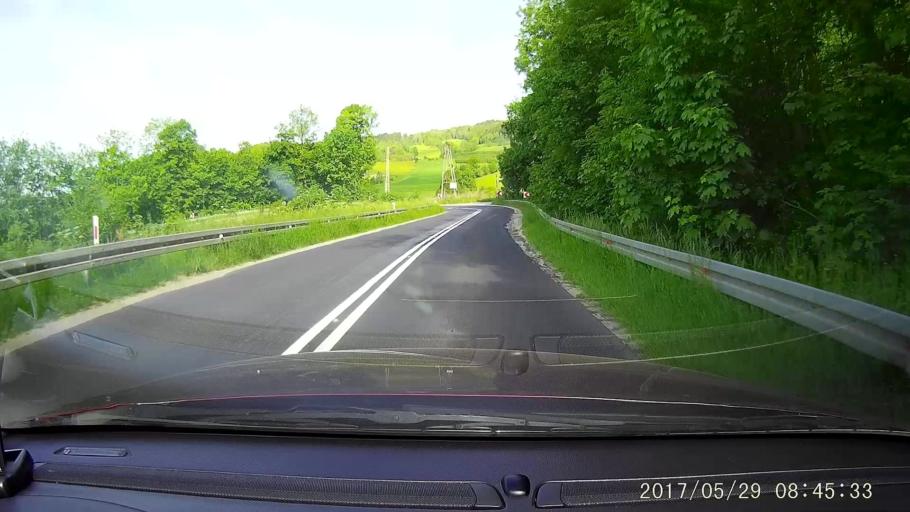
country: PL
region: Lower Silesian Voivodeship
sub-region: Powiat jeleniogorski
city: Jezow Sudecki
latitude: 50.9518
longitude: 15.8110
